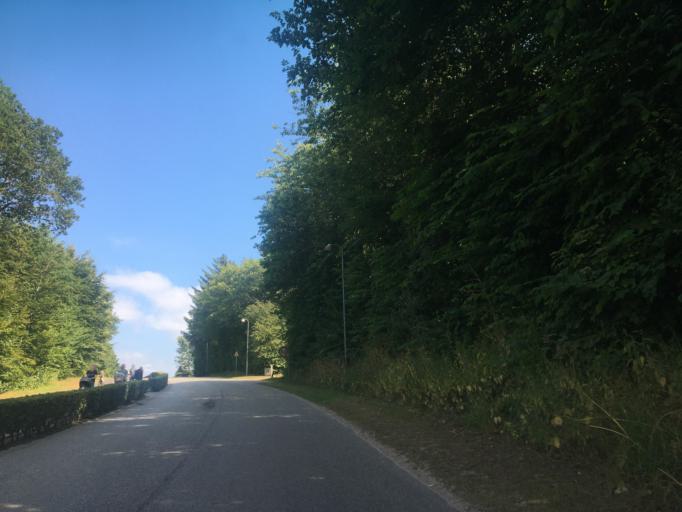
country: DK
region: North Denmark
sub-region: Morso Kommune
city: Nykobing Mors
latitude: 56.7634
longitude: 8.8179
